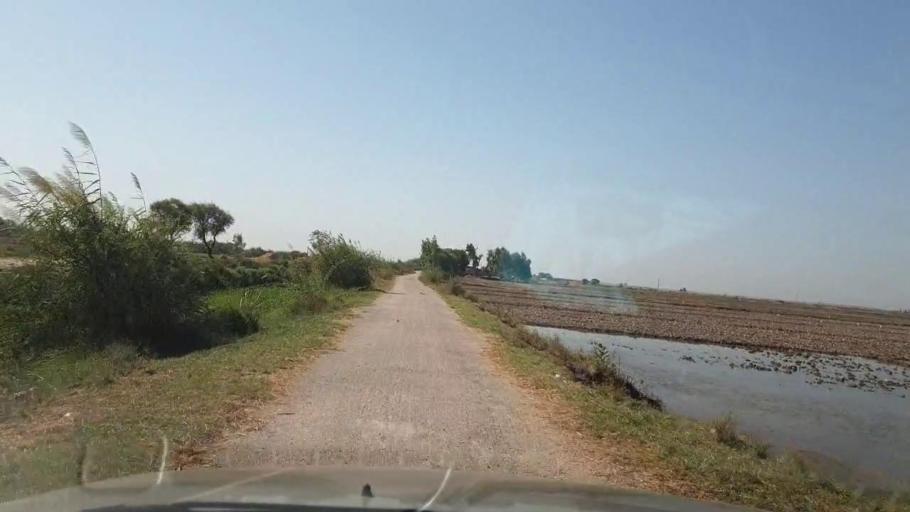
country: PK
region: Sindh
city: Thatta
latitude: 24.7223
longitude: 67.9221
